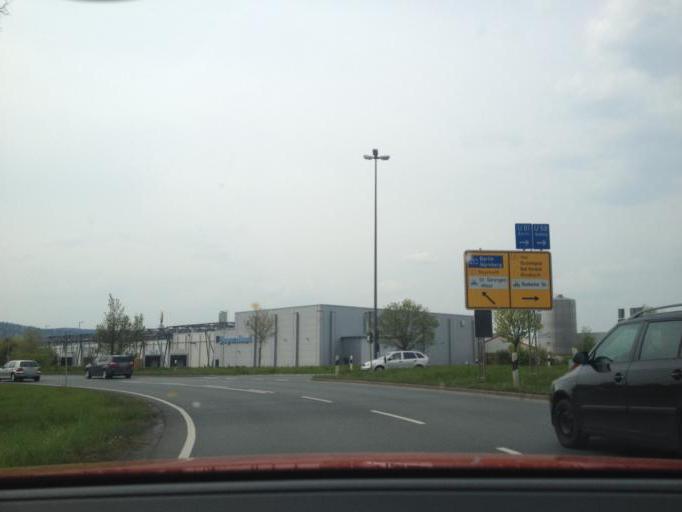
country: DE
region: Bavaria
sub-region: Upper Franconia
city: Bindlach
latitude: 49.9639
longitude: 11.6094
